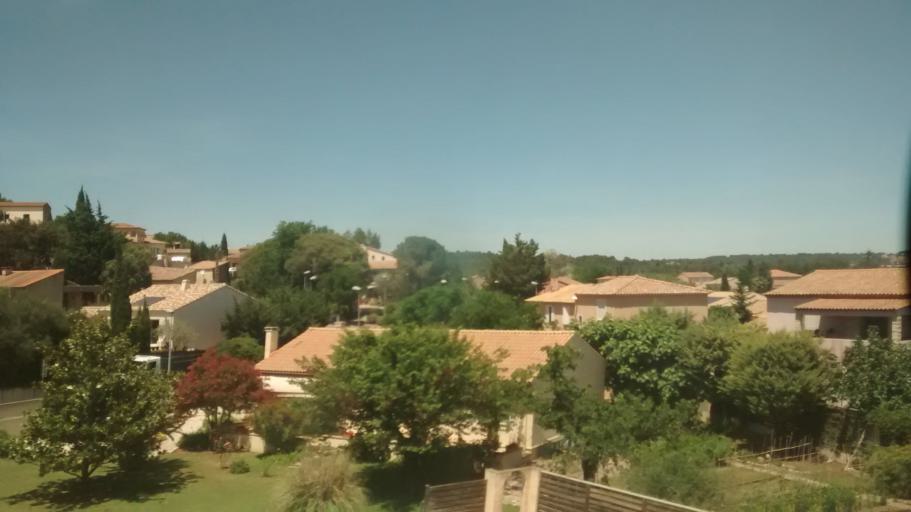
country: FR
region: Languedoc-Roussillon
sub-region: Departement du Gard
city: Milhaud
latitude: 43.7949
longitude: 4.3105
